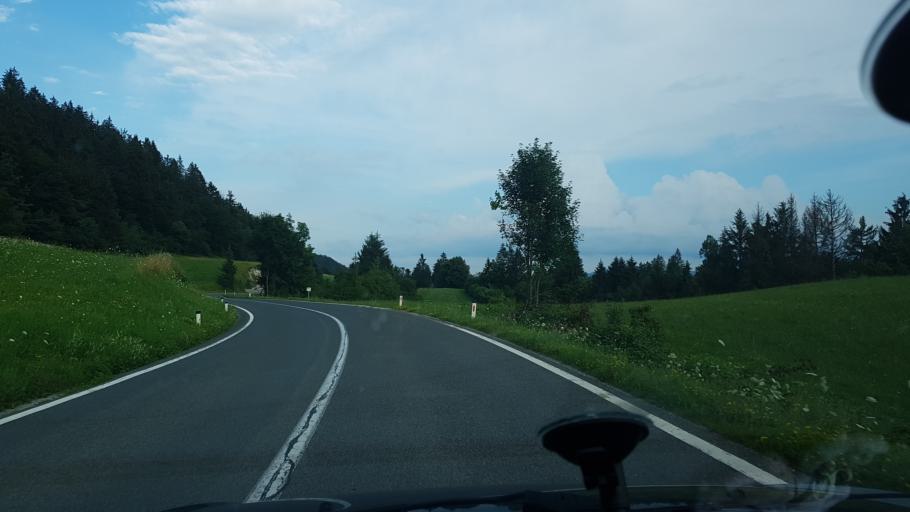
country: SI
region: Idrija
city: Idrija
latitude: 45.9535
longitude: 14.1015
